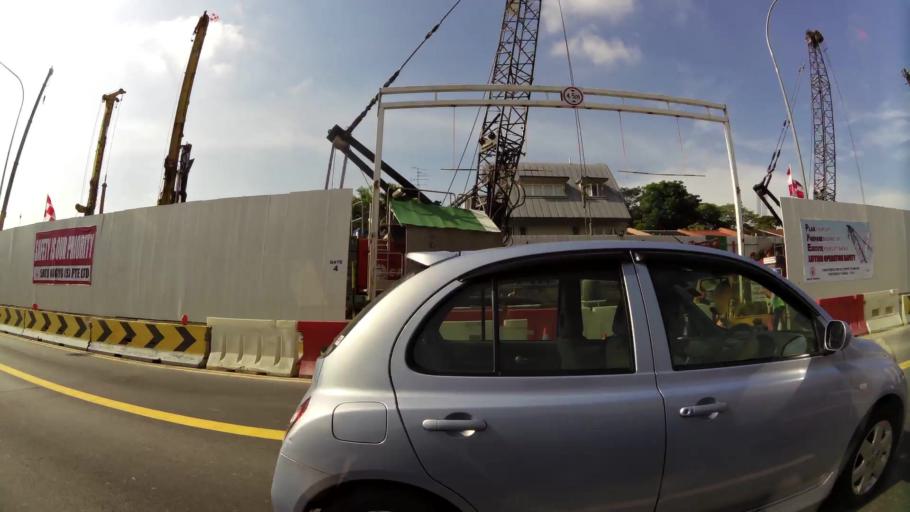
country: SG
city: Singapore
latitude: 1.3545
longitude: 103.8330
